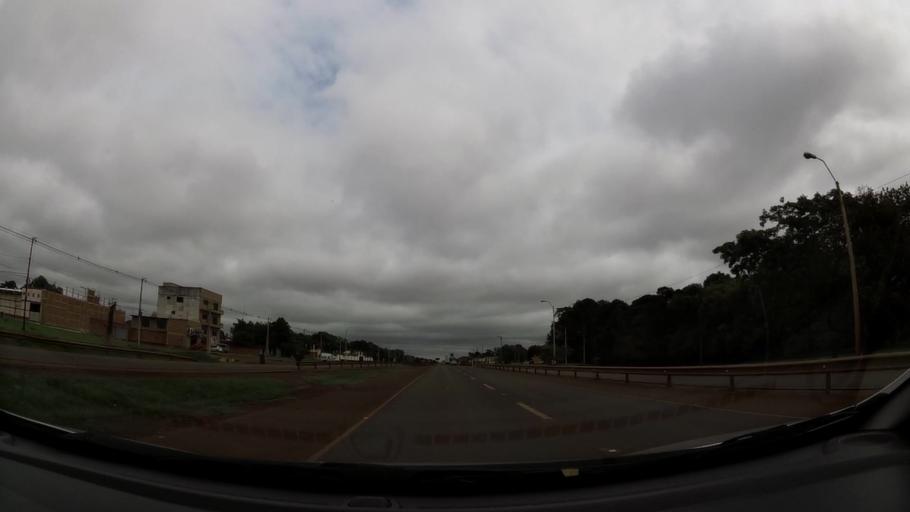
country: PY
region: Alto Parana
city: Presidente Franco
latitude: -25.4915
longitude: -54.7466
